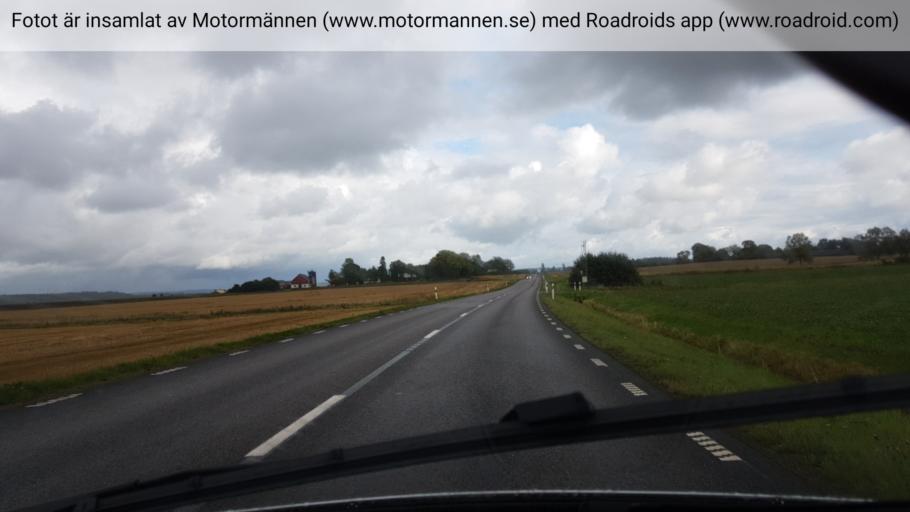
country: SE
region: Joenkoeping
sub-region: Mullsjo Kommun
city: Mullsjoe
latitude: 58.0800
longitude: 13.7834
